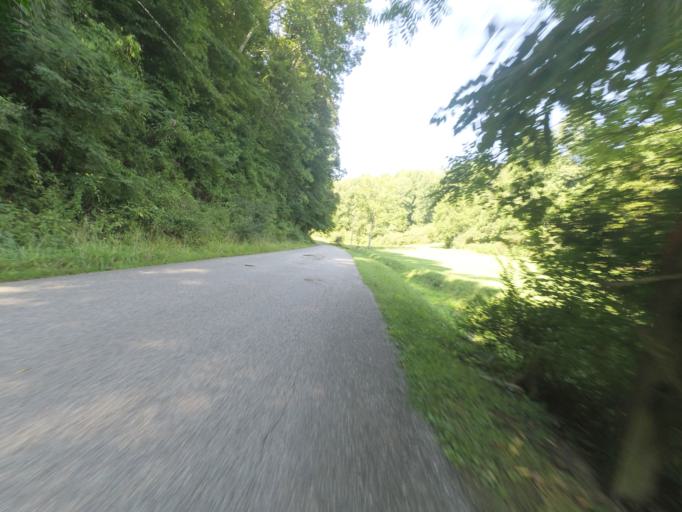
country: US
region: West Virginia
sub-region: Cabell County
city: Huntington
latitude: 38.3726
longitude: -82.4667
